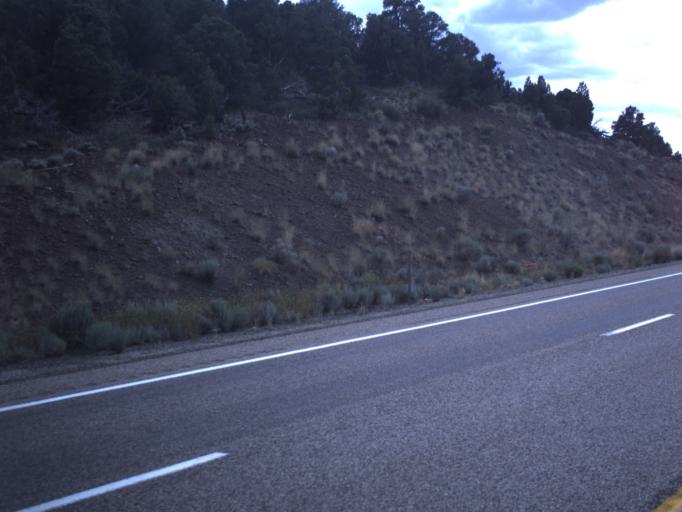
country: US
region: Utah
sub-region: Beaver County
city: Beaver
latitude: 38.0610
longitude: -112.6266
